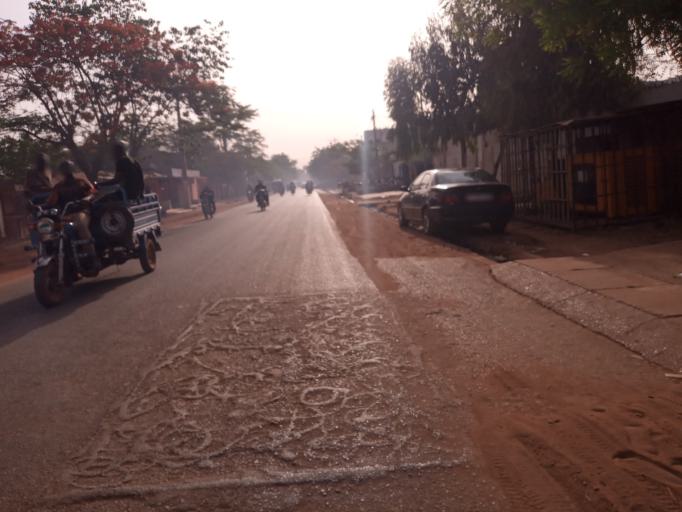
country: ML
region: Bamako
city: Bamako
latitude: 12.6654
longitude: -7.9728
